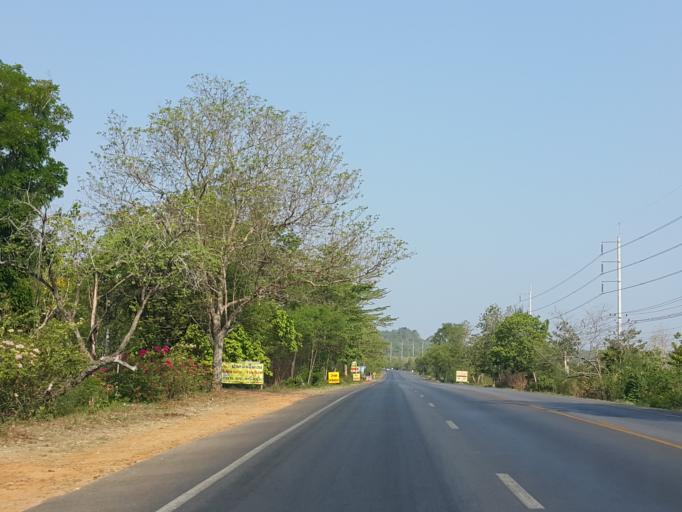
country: TH
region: Kanchanaburi
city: Sai Yok
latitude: 14.1106
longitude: 99.2101
